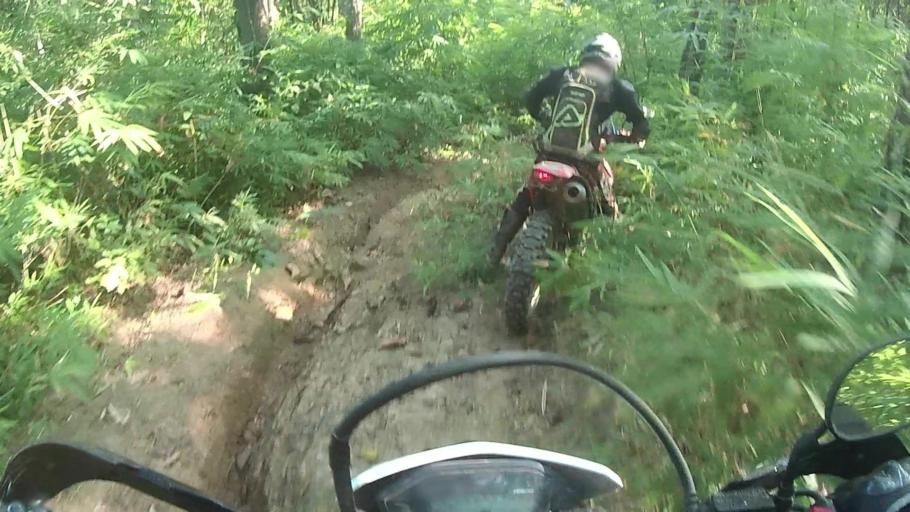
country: TH
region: Chiang Mai
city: Mae Taeng
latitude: 18.9571
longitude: 98.8712
